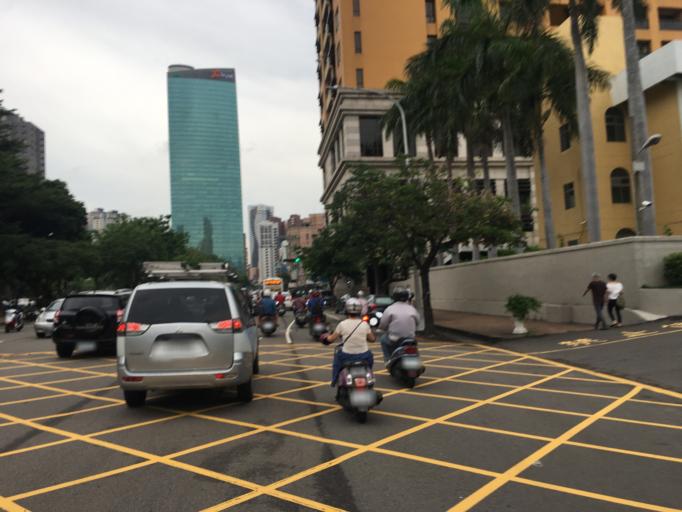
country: TW
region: Taiwan
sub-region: Taichung City
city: Taichung
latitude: 24.1459
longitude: 120.6654
